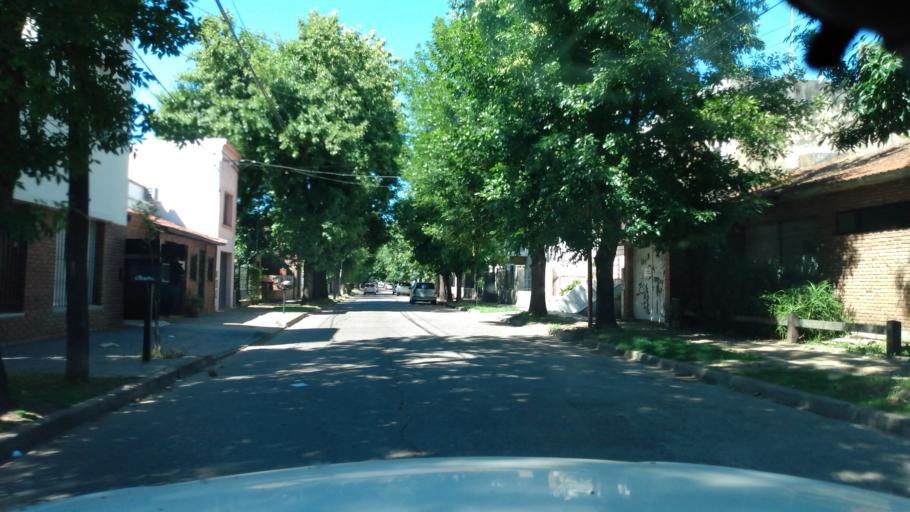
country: AR
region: Buenos Aires
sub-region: Partido de Lujan
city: Lujan
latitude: -34.5663
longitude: -59.1089
